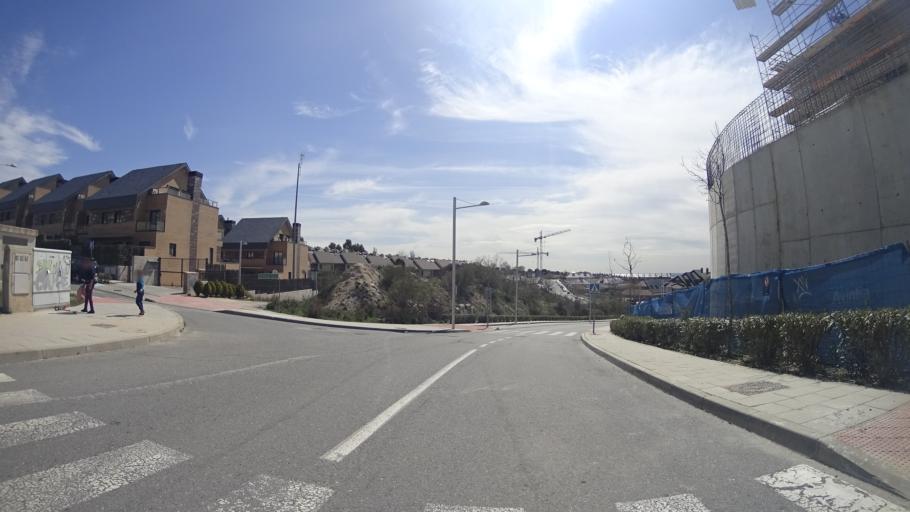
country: ES
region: Madrid
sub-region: Provincia de Madrid
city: Torrelodones
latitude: 40.5666
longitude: -3.9192
